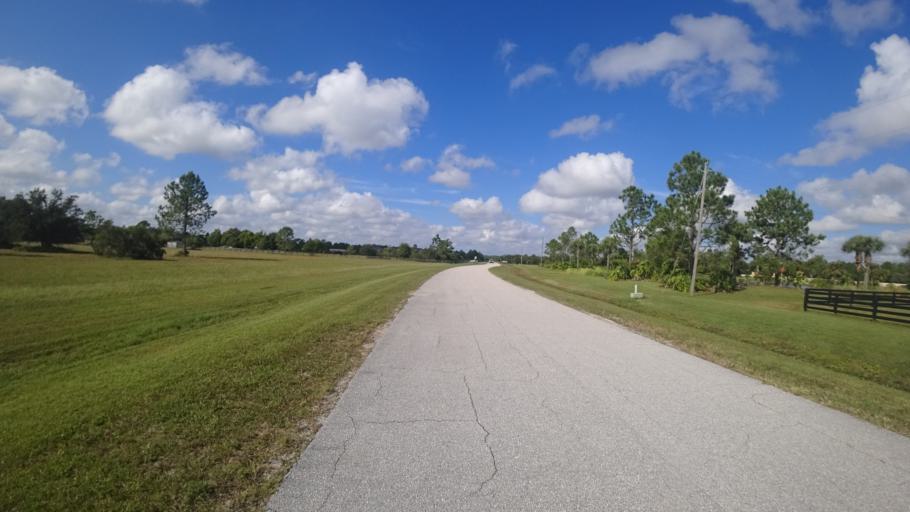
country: US
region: Florida
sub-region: Sarasota County
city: The Meadows
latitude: 27.4023
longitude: -82.3303
